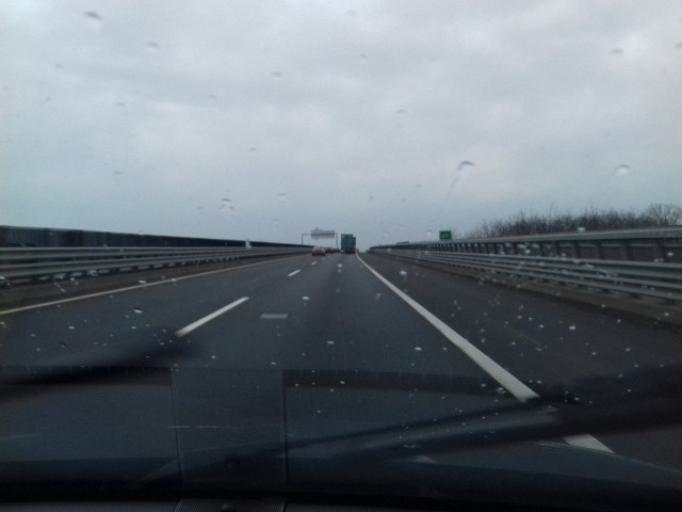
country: HU
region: Szabolcs-Szatmar-Bereg
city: Nagykallo
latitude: 47.8893
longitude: 21.7816
